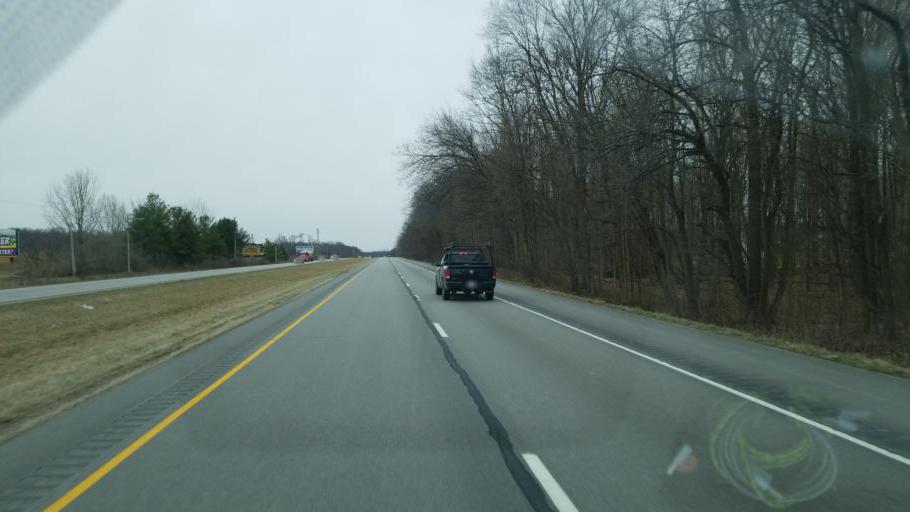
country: US
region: Indiana
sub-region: Marshall County
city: Plymouth
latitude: 41.3123
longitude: -86.2756
